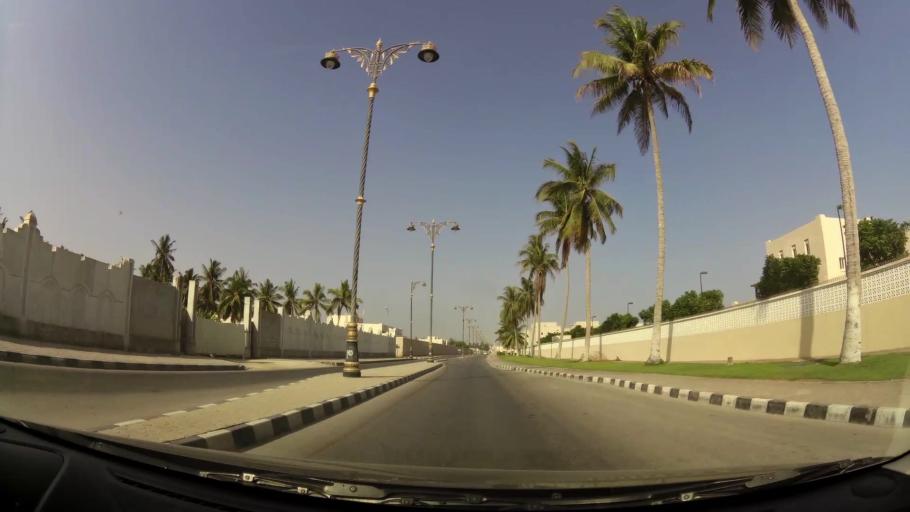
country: OM
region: Zufar
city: Salalah
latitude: 17.0011
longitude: 54.0932
